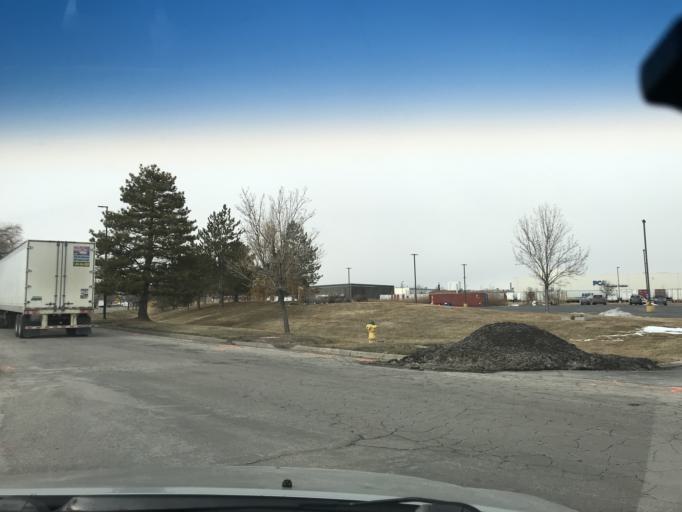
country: US
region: Utah
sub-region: Salt Lake County
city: West Valley City
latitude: 40.7765
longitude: -112.0269
